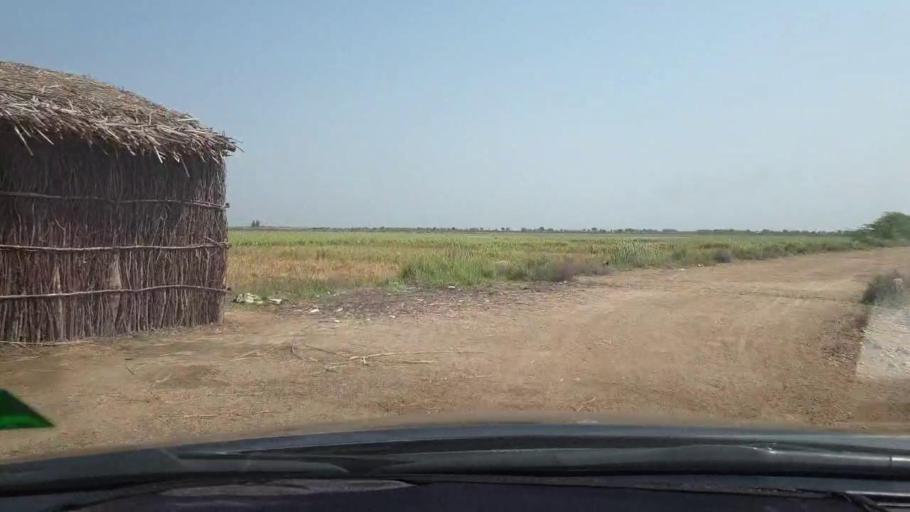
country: PK
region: Sindh
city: Tando Bago
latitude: 24.7935
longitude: 69.0818
